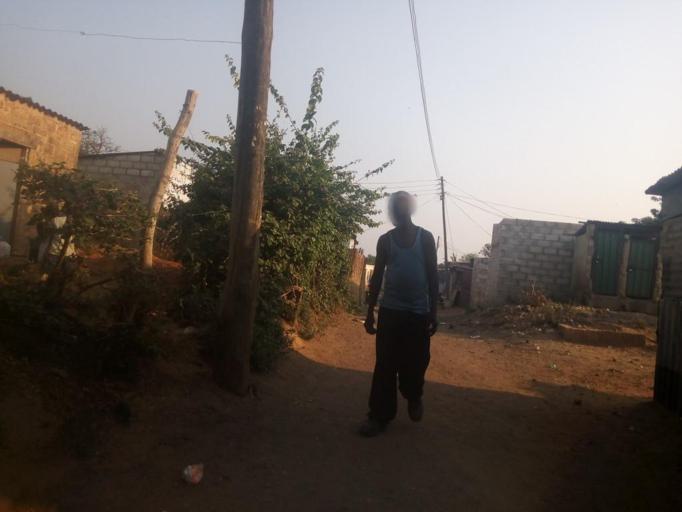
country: ZM
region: Lusaka
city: Lusaka
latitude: -15.4055
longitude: 28.3635
